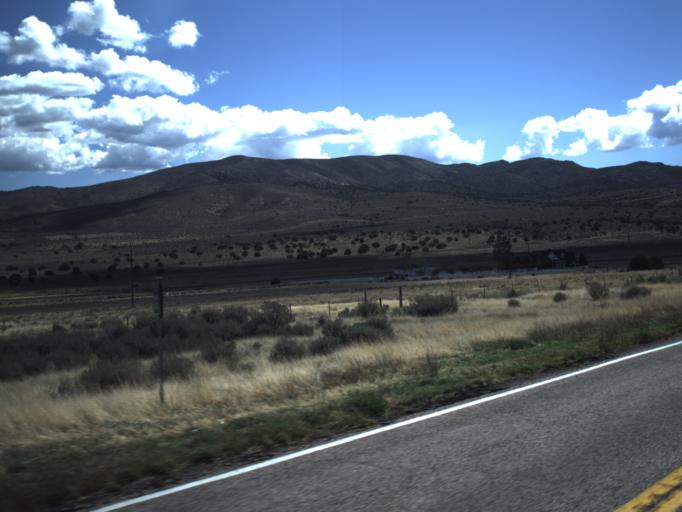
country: US
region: Utah
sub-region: Washington County
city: Enterprise
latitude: 37.5134
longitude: -113.6341
